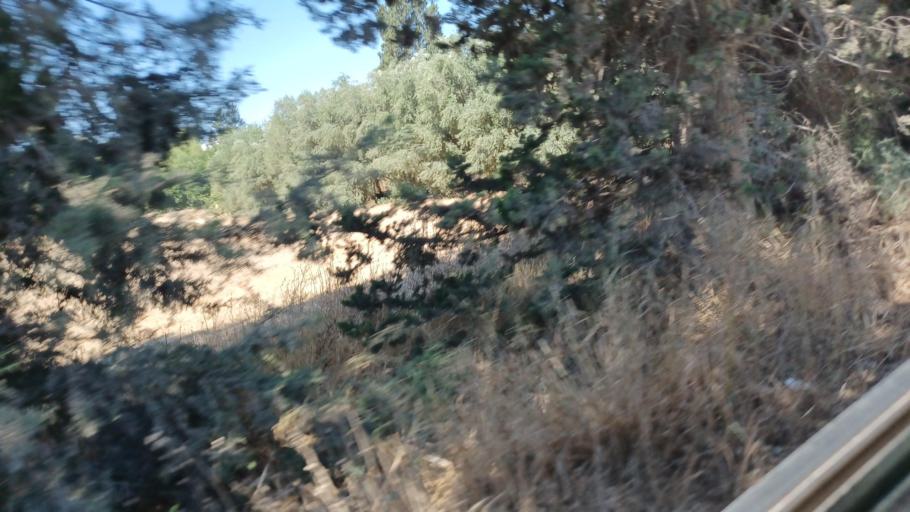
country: CY
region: Ammochostos
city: Acheritou
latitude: 35.0834
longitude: 33.8879
